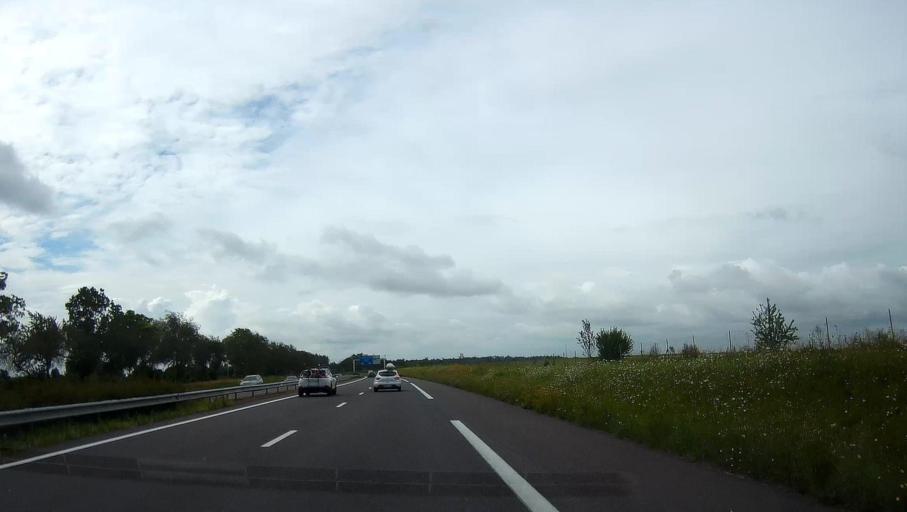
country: FR
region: Champagne-Ardenne
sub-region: Departement de la Marne
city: Fagnieres
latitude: 48.9769
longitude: 4.2859
